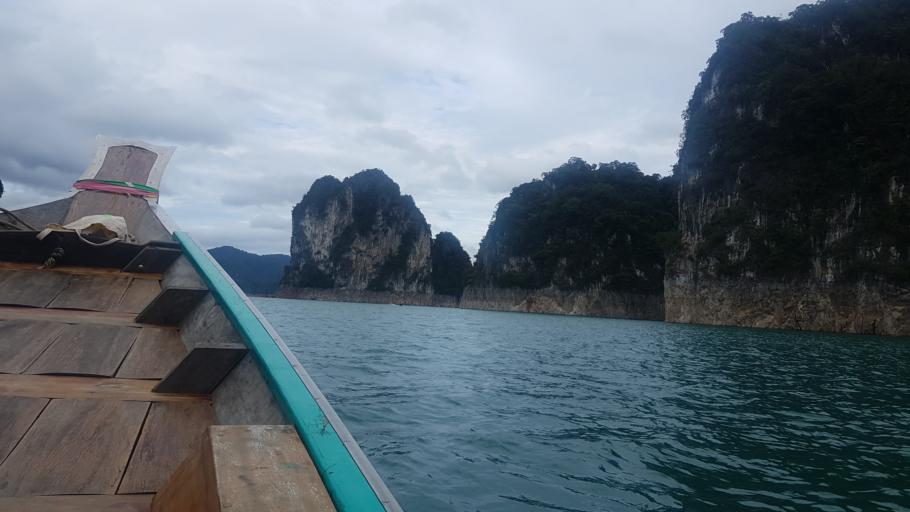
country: TH
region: Surat Thani
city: Phanom
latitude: 9.0171
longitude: 98.7367
